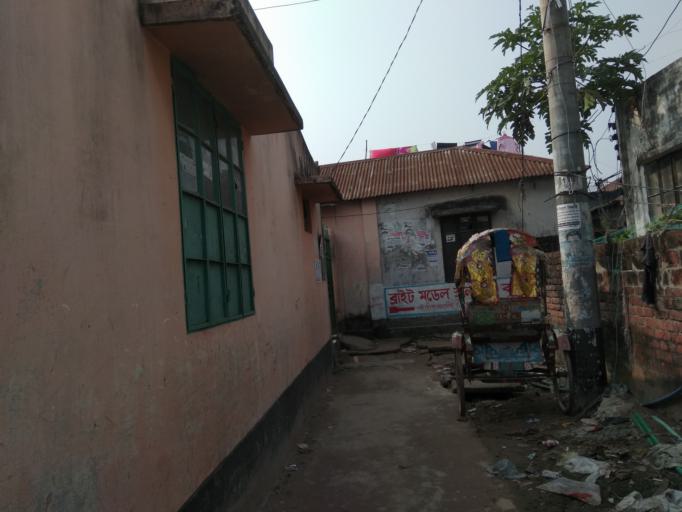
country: BD
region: Dhaka
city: Tungi
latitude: 23.8596
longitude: 90.3857
